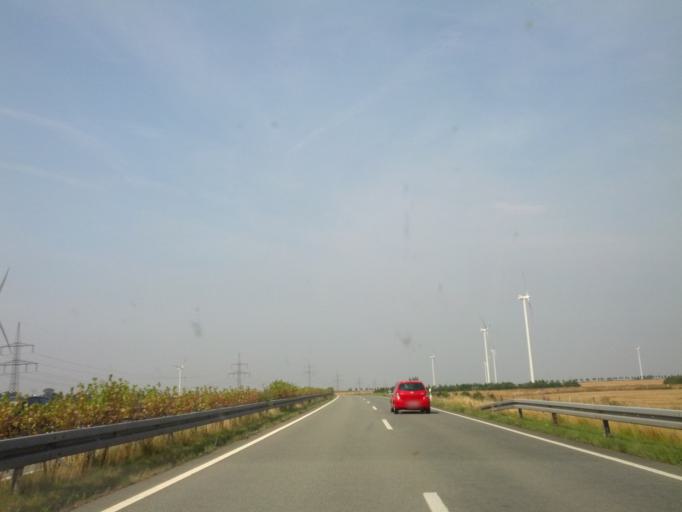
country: DE
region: Mecklenburg-Vorpommern
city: Brandshagen
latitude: 54.1768
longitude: 13.1734
